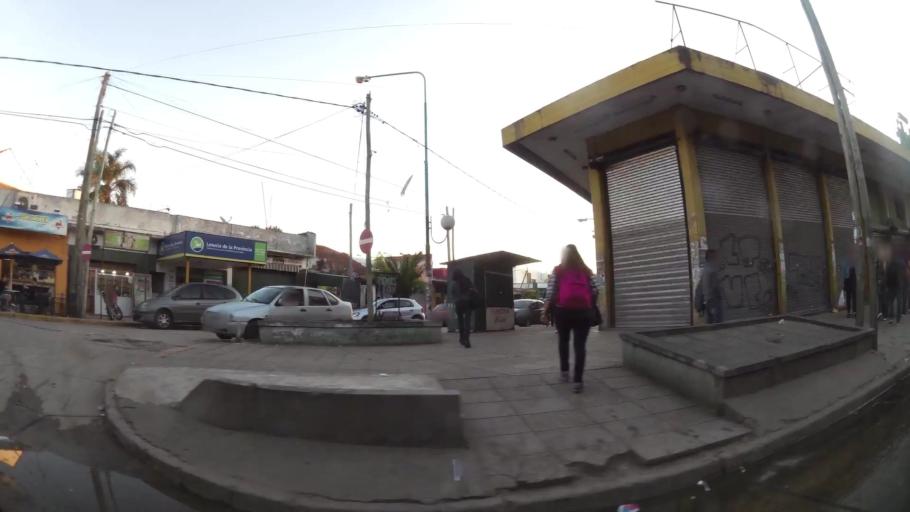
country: AR
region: Buenos Aires
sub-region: Partido de Almirante Brown
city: Adrogue
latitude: -34.8020
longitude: -58.3374
